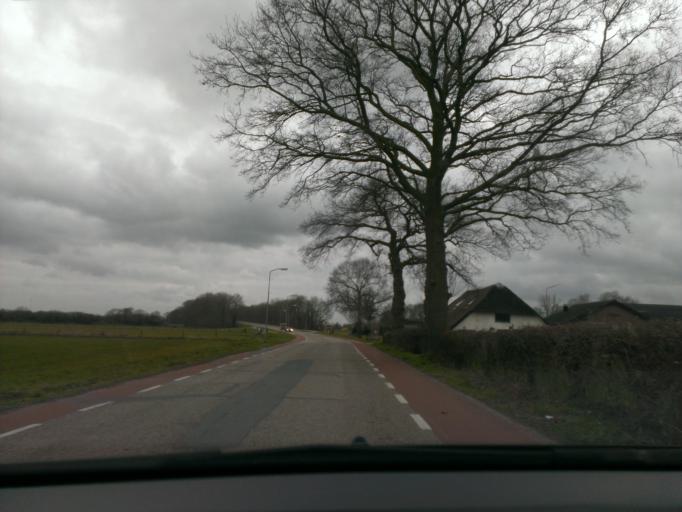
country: NL
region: Gelderland
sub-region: Gemeente Voorst
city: Twello
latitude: 52.2082
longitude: 6.0721
